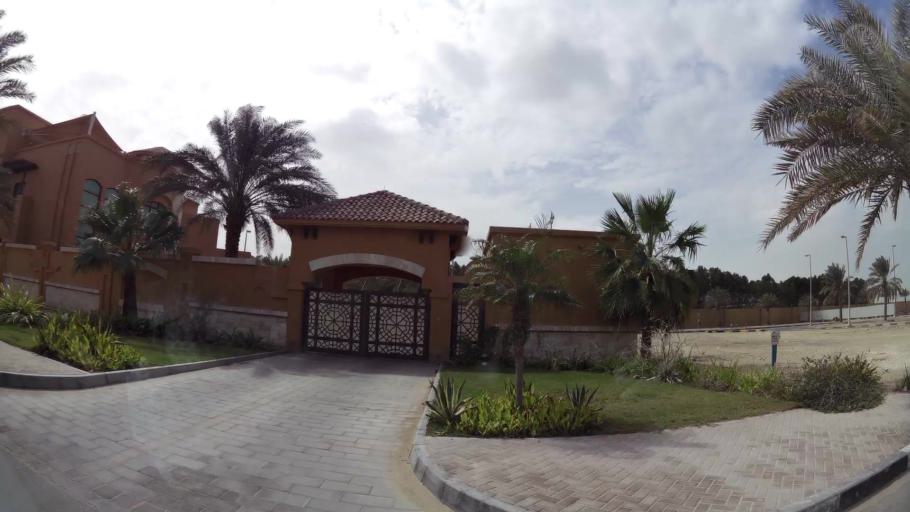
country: AE
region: Abu Dhabi
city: Abu Dhabi
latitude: 24.3989
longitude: 54.4860
